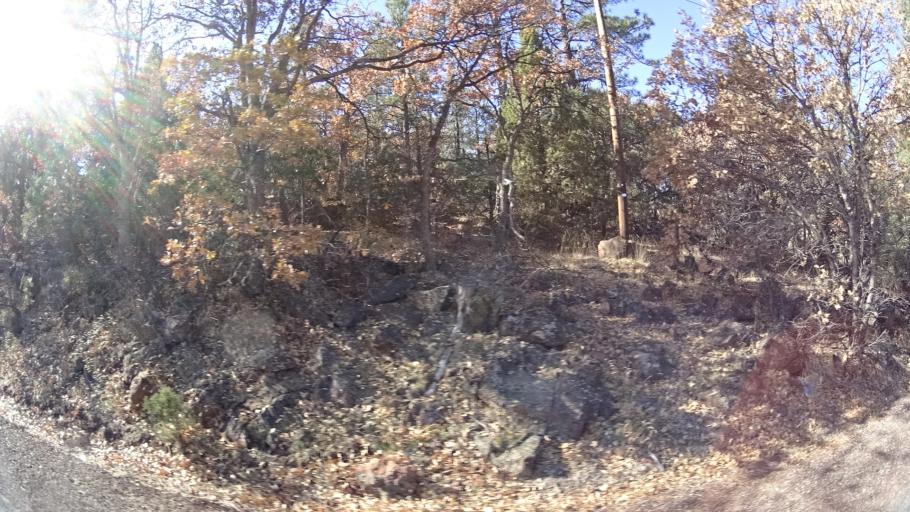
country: US
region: California
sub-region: Siskiyou County
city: Weed
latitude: 41.4956
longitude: -122.5113
